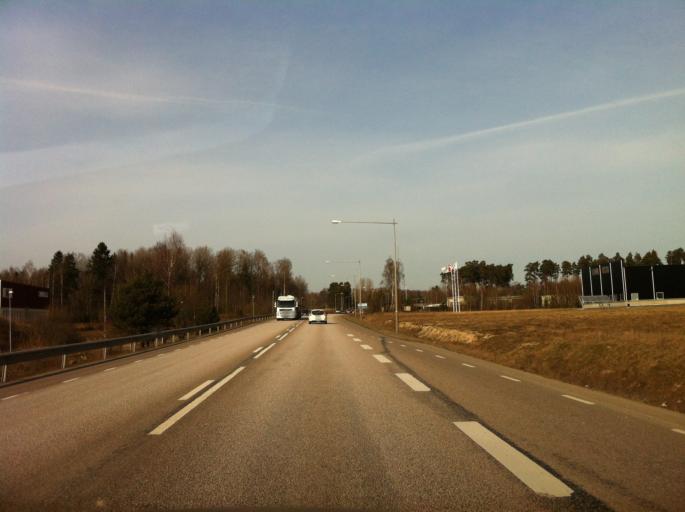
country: SE
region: Vaestra Goetaland
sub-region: Skovde Kommun
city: Skoevde
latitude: 58.3964
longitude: 13.8730
